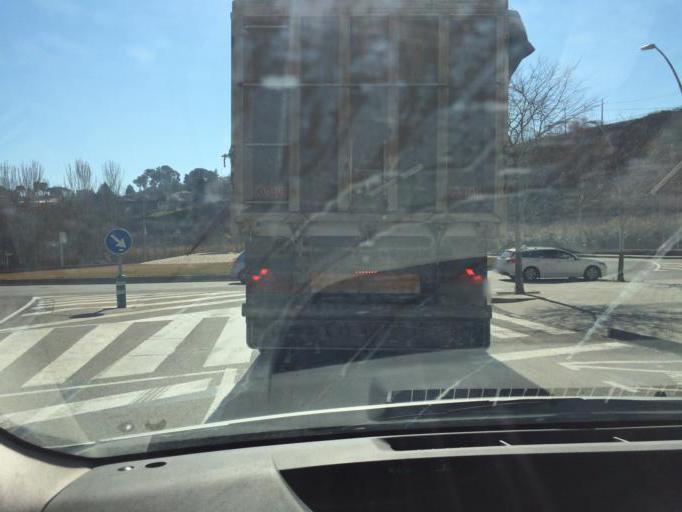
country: ES
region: Catalonia
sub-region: Provincia de Barcelona
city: Manresa
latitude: 41.7215
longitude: 1.8160
